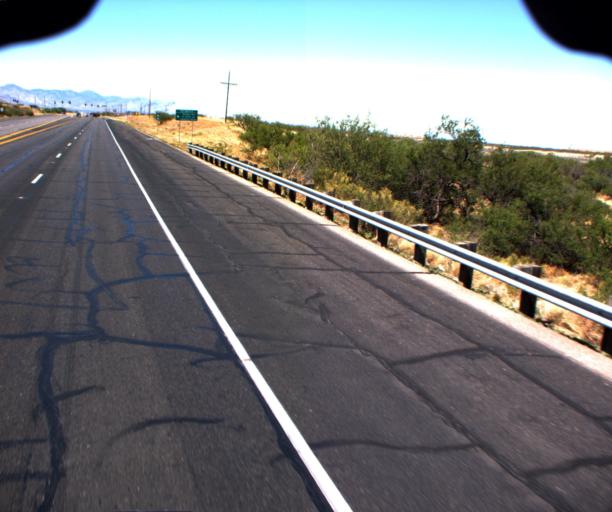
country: US
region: Arizona
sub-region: Cochise County
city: Sierra Vista
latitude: 31.5711
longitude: -110.3139
